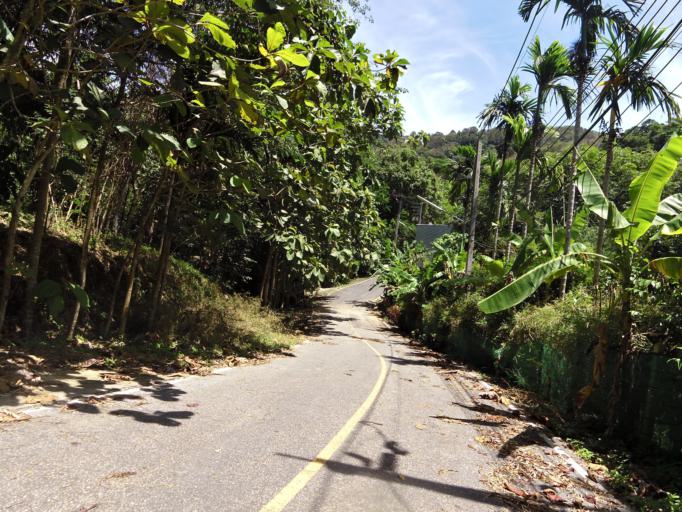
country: TH
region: Phuket
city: Ban Karon
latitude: 7.8471
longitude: 98.3077
